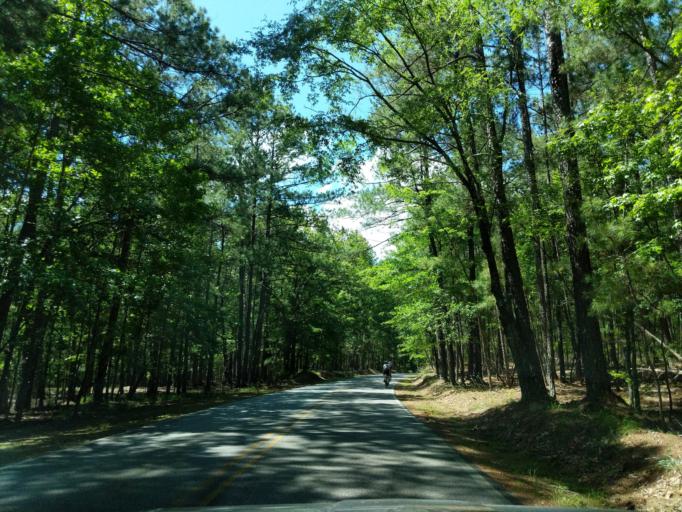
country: US
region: Georgia
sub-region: Columbia County
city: Appling
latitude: 33.6561
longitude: -82.3876
